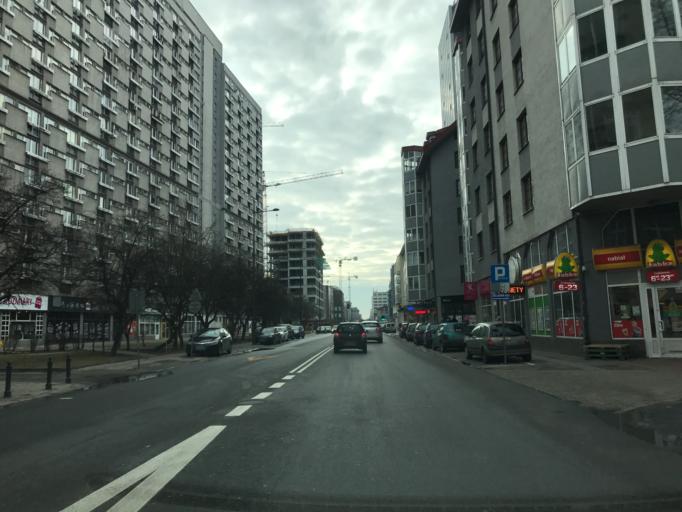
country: PL
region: Masovian Voivodeship
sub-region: Warszawa
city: Wola
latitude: 52.2360
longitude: 20.9898
